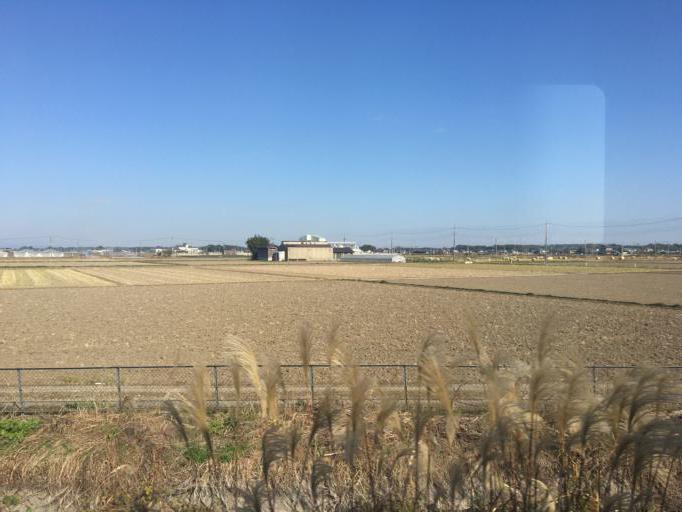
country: JP
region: Tochigi
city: Oyama
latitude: 36.3467
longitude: 139.7901
